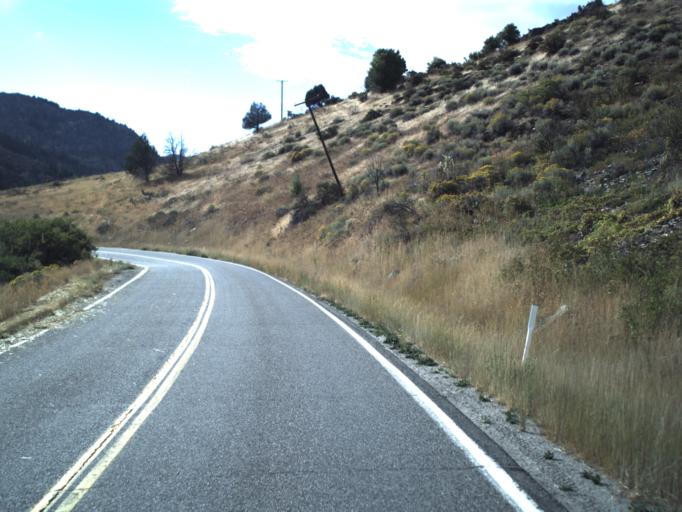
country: US
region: Utah
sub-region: Cache County
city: Millville
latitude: 41.6179
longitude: -111.6453
